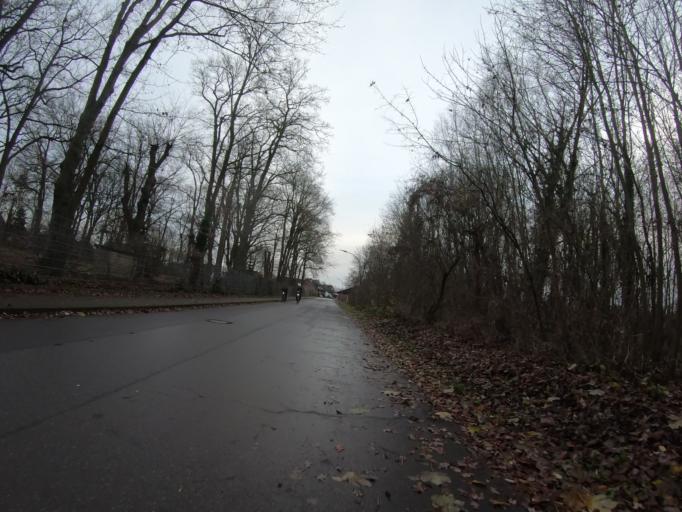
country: DE
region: Lower Saxony
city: Isenbuttel
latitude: 52.4291
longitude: 10.5793
